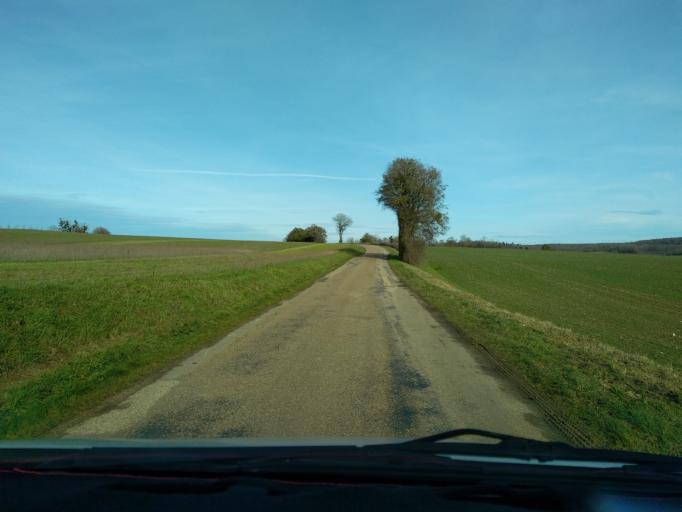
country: FR
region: Franche-Comte
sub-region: Departement de la Haute-Saone
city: Marnay
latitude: 47.3136
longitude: 5.6785
